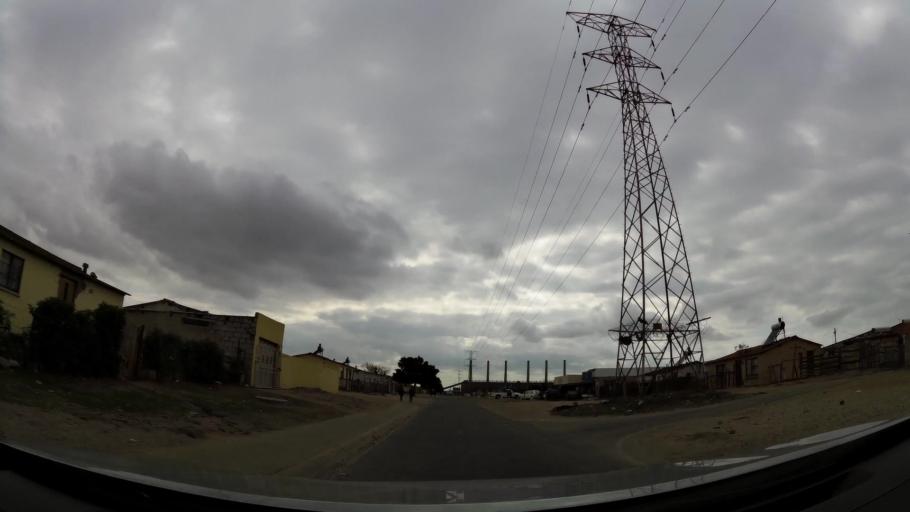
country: ZA
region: Eastern Cape
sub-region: Nelson Mandela Bay Metropolitan Municipality
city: Port Elizabeth
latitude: -33.8795
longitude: 25.5965
